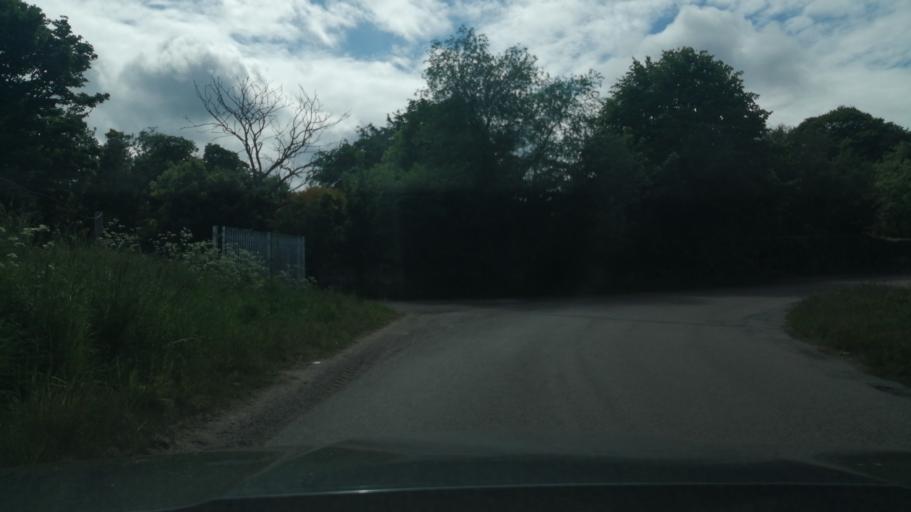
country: GB
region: Scotland
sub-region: Moray
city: Elgin
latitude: 57.6536
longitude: -3.2812
